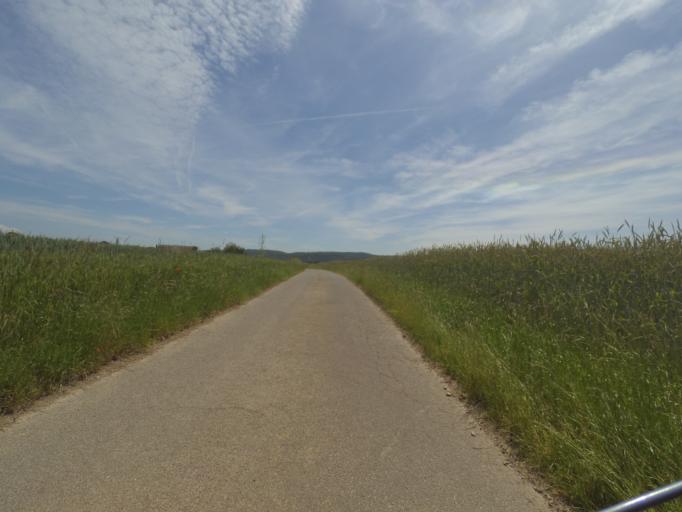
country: DE
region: Rheinland-Pfalz
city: Kobern-Gondorf
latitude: 50.2986
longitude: 7.4486
